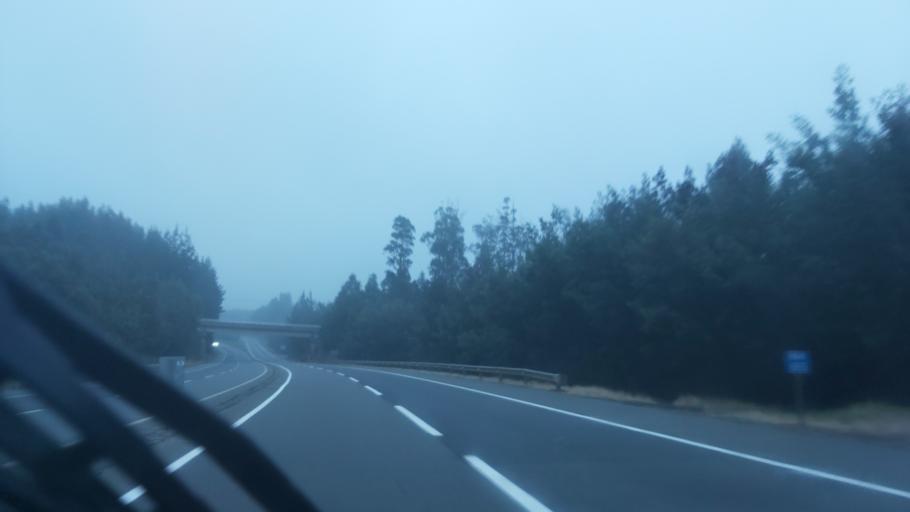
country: CL
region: Biobio
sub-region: Provincia de Concepcion
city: Penco
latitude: -36.7427
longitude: -72.9113
